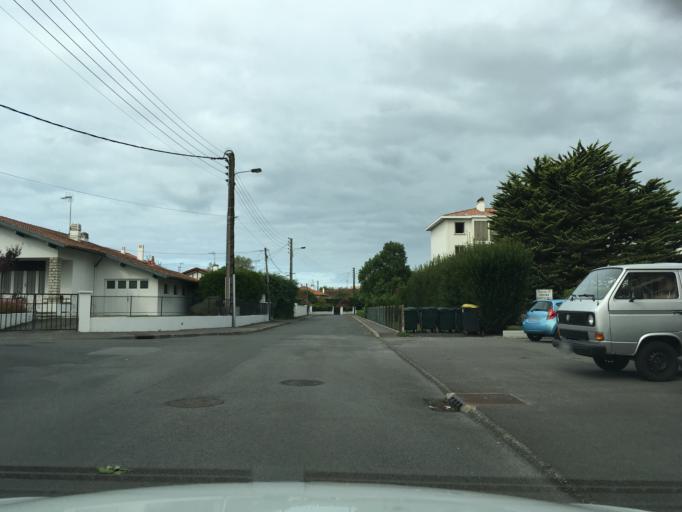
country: FR
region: Aquitaine
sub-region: Departement des Pyrenees-Atlantiques
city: Anglet
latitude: 43.4990
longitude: -1.5078
